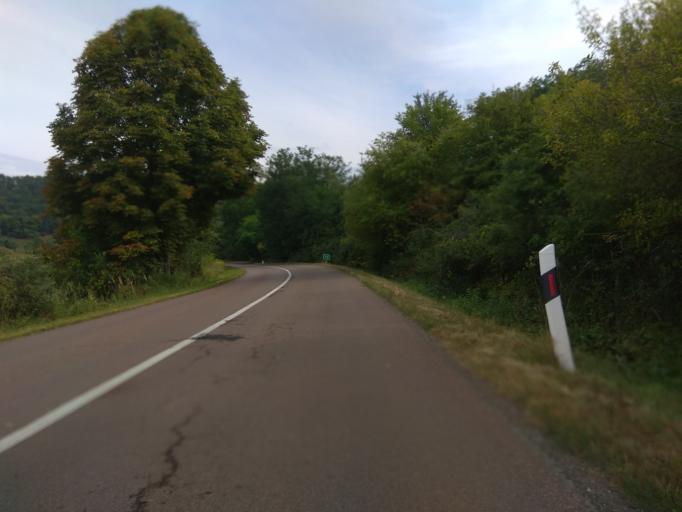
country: HU
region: Heves
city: Belapatfalva
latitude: 48.0209
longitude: 20.2926
